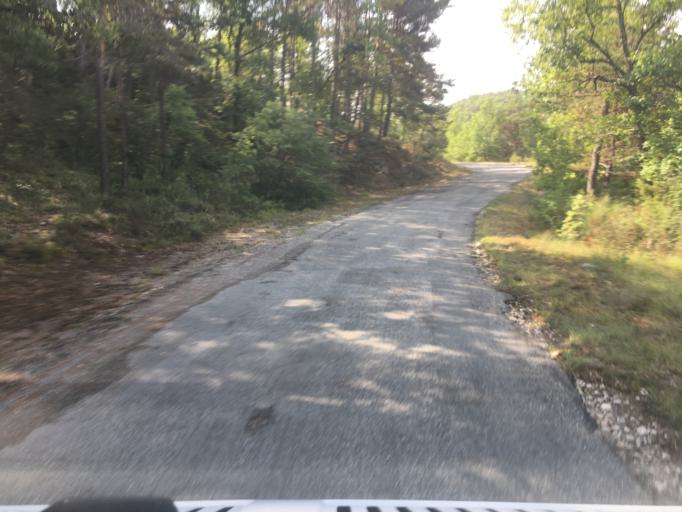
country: FR
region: Provence-Alpes-Cote d'Azur
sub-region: Departement des Alpes-de-Haute-Provence
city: Mallemoisson
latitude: 43.9262
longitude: 6.1909
